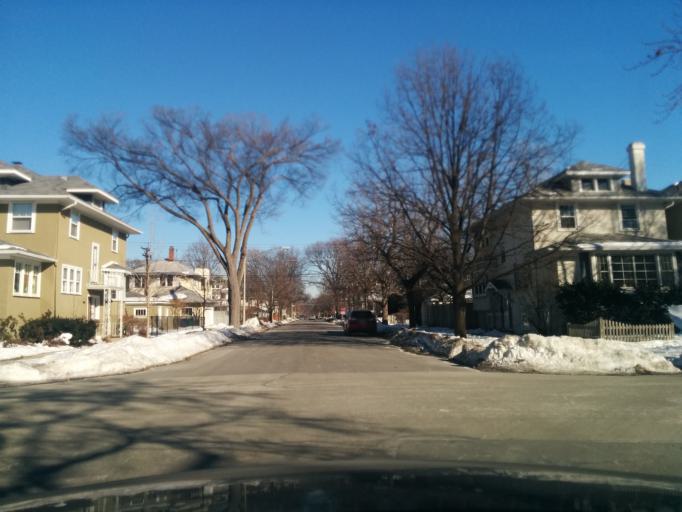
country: US
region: Illinois
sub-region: Cook County
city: Oak Park
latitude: 41.8744
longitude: -87.7881
